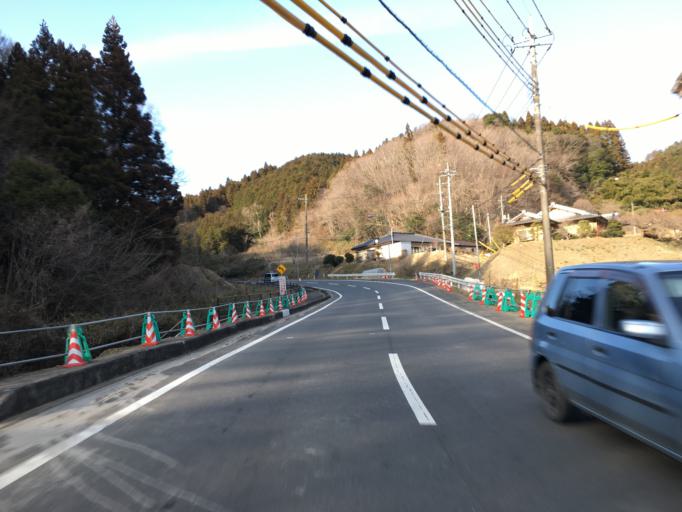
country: JP
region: Ibaraki
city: Daigo
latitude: 36.7456
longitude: 140.4533
